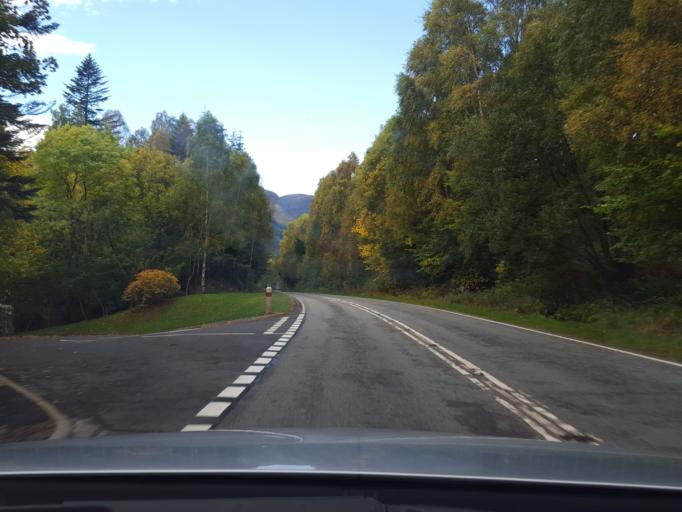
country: GB
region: Scotland
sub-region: Highland
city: Fort William
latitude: 57.2397
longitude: -5.4477
